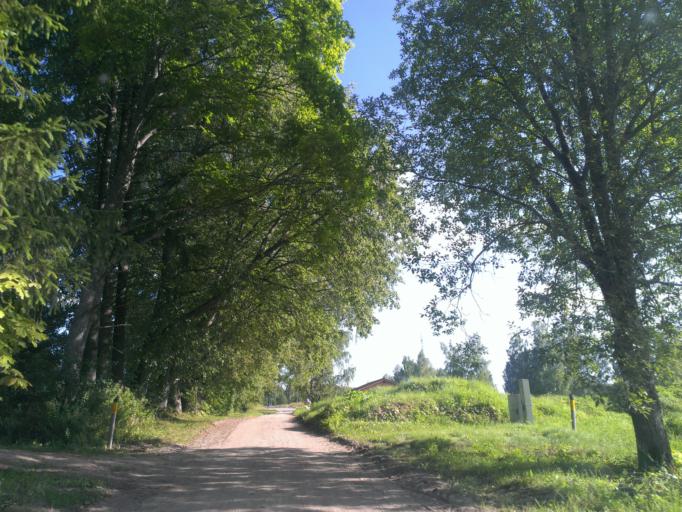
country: LV
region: Sigulda
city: Sigulda
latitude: 57.1685
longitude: 24.8758
